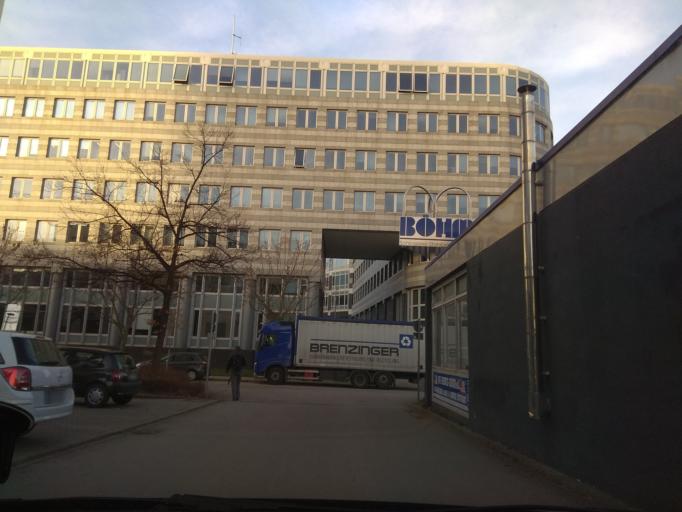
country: DE
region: Baden-Wuerttemberg
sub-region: Regierungsbezirk Stuttgart
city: Leinfelden-Echterdingen
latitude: 48.7263
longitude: 9.1187
